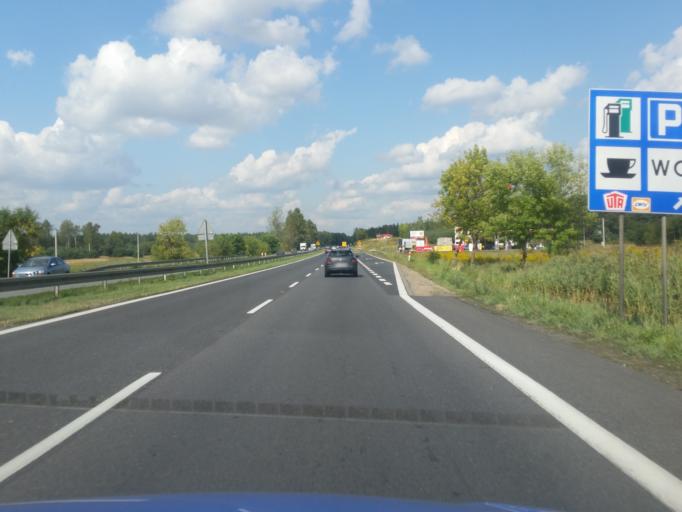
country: PL
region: Silesian Voivodeship
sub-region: Powiat bedzinski
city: Siewierz
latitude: 50.5104
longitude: 19.1960
